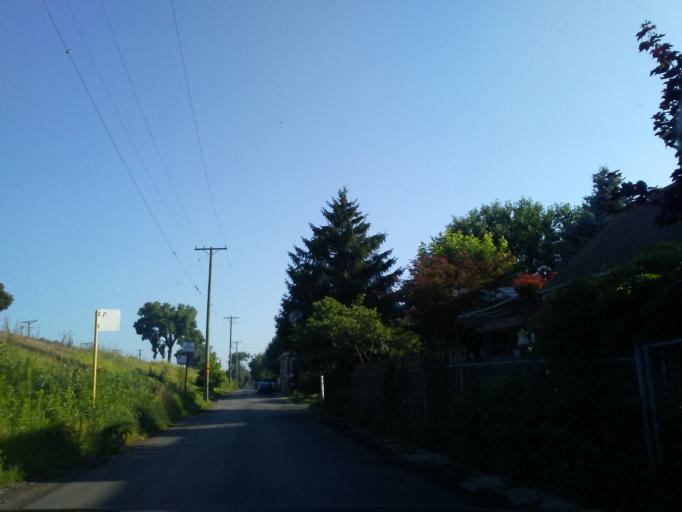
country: US
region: Illinois
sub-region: Cook County
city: Oak Park
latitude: 41.9259
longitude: -87.7414
